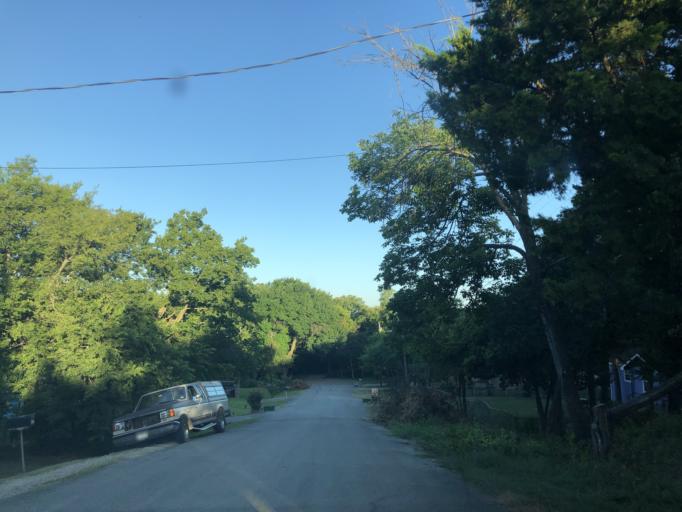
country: US
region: Texas
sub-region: Dallas County
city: Duncanville
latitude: 32.6395
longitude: -96.9109
